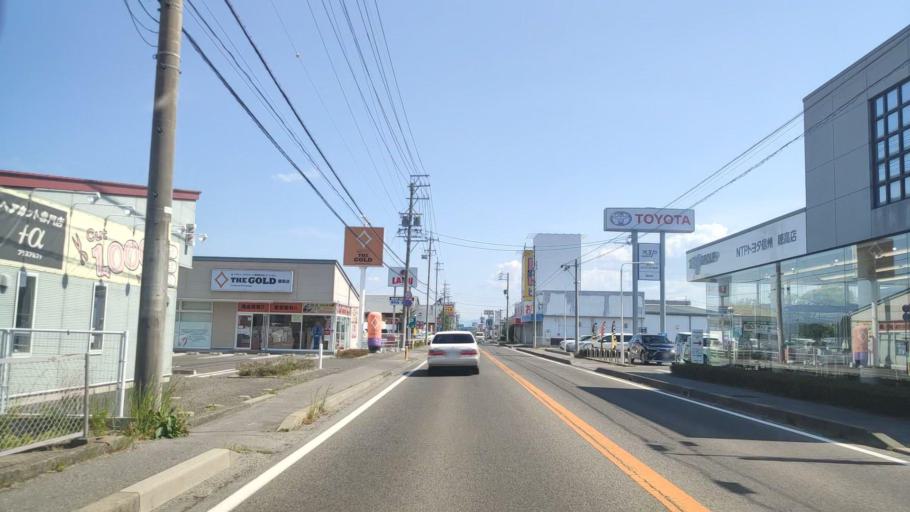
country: JP
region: Nagano
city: Hotaka
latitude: 36.3306
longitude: 137.8917
